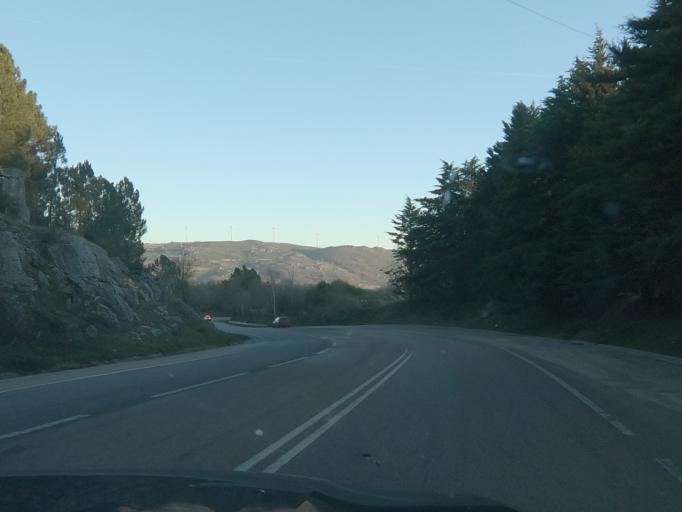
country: PT
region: Vila Real
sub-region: Vila Pouca de Aguiar
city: Vila Pouca de Aguiar
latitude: 41.4908
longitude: -7.6688
